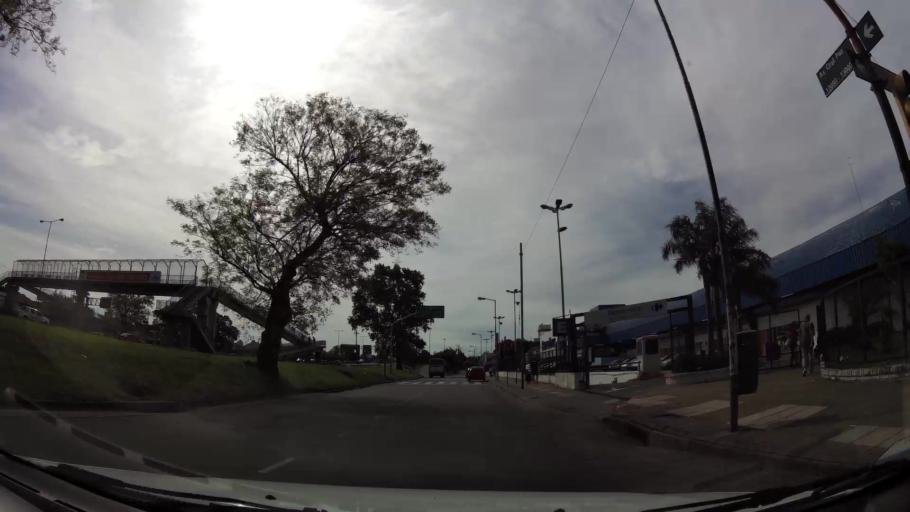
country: AR
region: Buenos Aires F.D.
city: Villa Lugano
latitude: -34.6647
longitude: -58.5140
